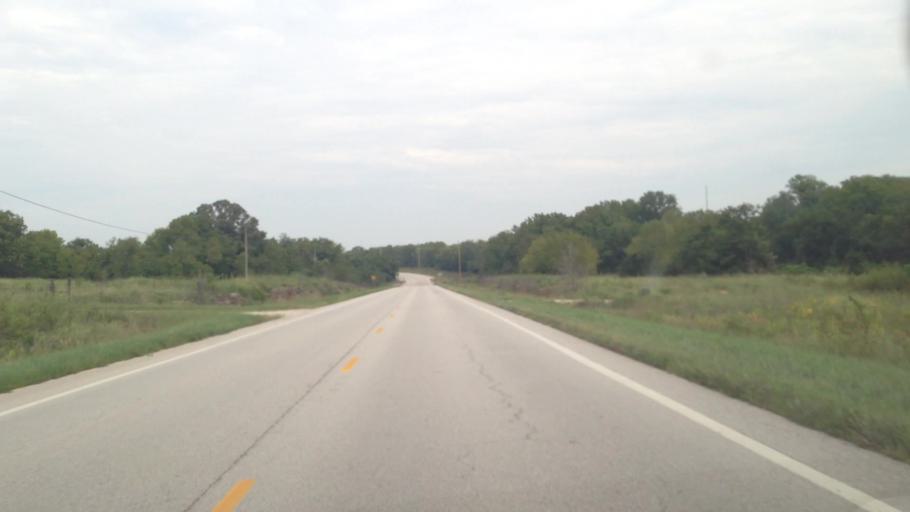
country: US
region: Kansas
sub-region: Allen County
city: Iola
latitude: 38.0349
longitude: -95.1723
